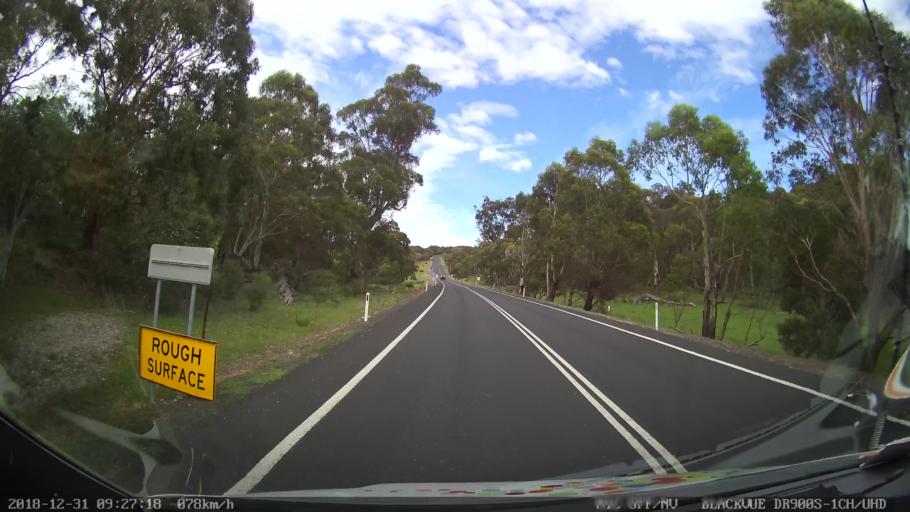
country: AU
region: New South Wales
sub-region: Snowy River
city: Jindabyne
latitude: -36.4552
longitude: 148.4865
